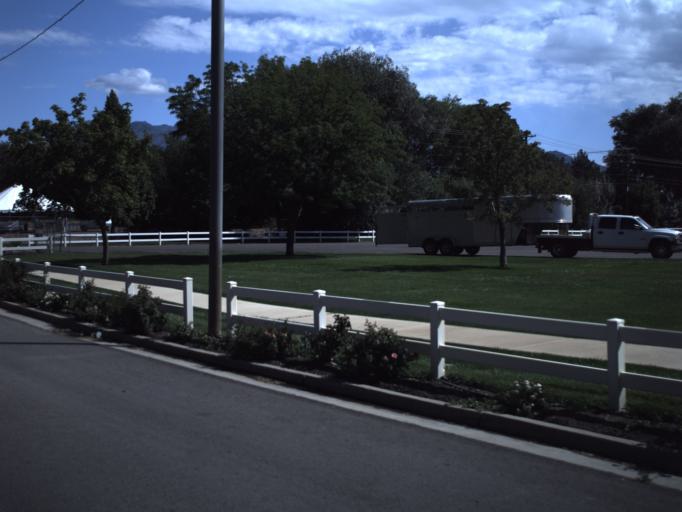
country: US
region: Utah
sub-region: Utah County
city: Spanish Fork
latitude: 40.1035
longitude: -111.6551
